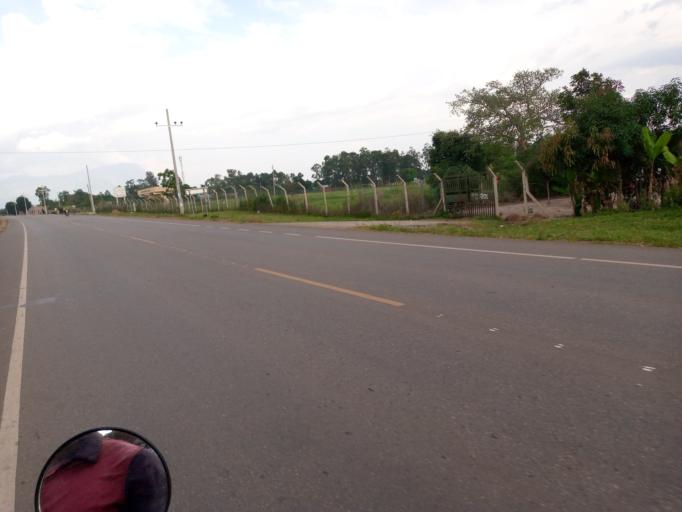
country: UG
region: Eastern Region
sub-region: Mbale District
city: Mbale
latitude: 1.0747
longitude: 34.1136
